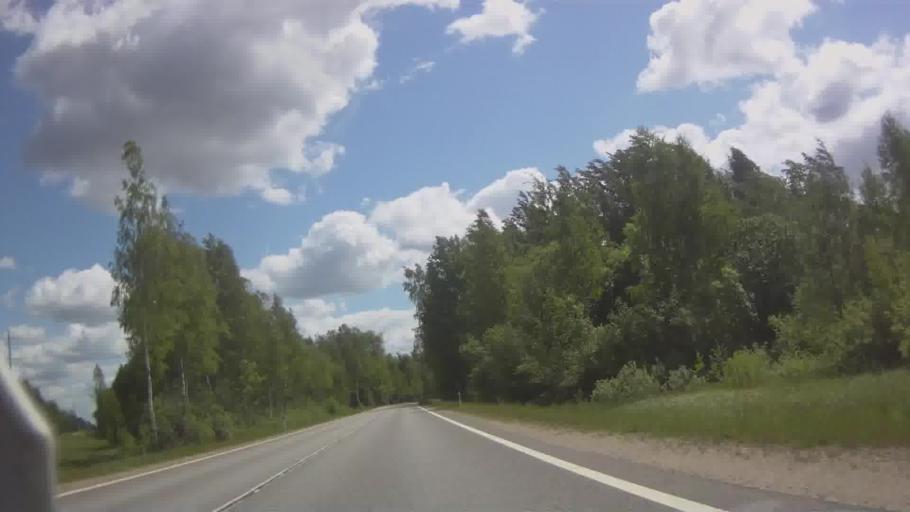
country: LV
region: Livani
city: Livani
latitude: 56.5291
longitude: 26.1487
